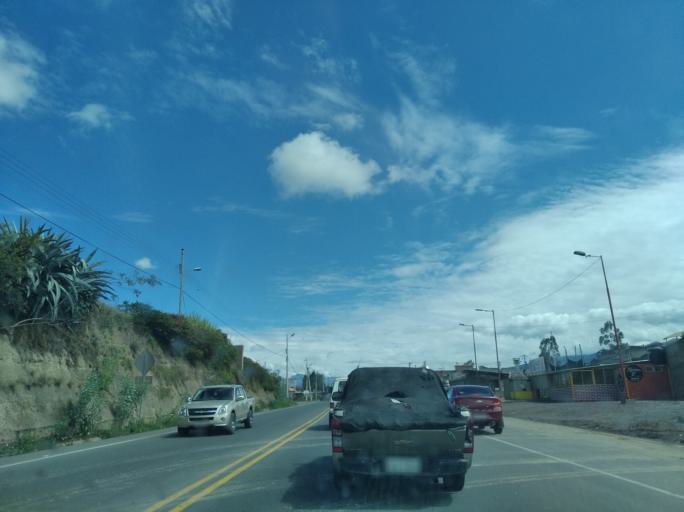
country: EC
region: Pichincha
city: Sangolqui
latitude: -0.1784
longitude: -78.3293
